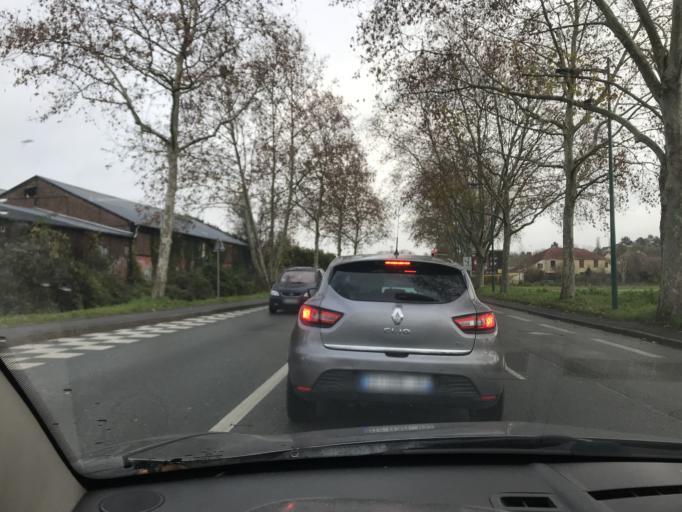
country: FR
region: Ile-de-France
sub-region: Departement du Val-d'Oise
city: Saint-Ouen-l'Aumone
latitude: 49.0525
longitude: 2.1156
